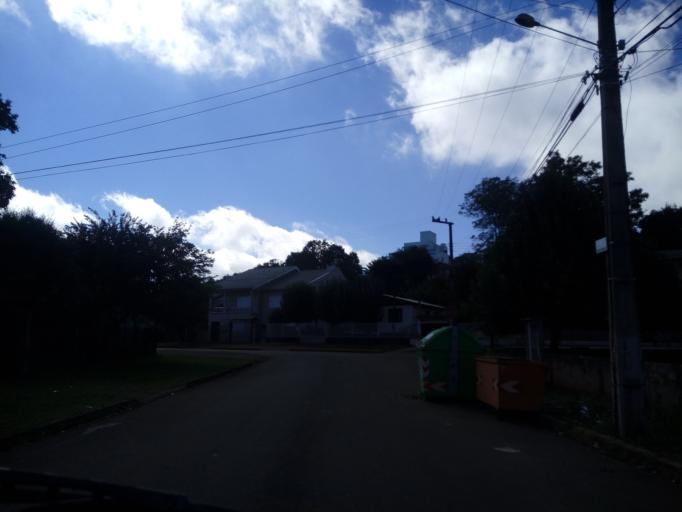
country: BR
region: Santa Catarina
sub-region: Chapeco
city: Chapeco
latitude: -27.1113
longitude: -52.6032
